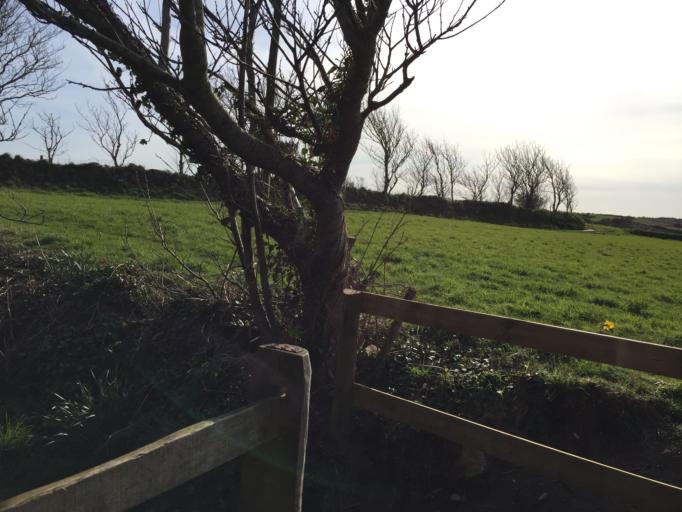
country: JE
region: St Helier
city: Saint Helier
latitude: 49.2504
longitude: -2.1708
